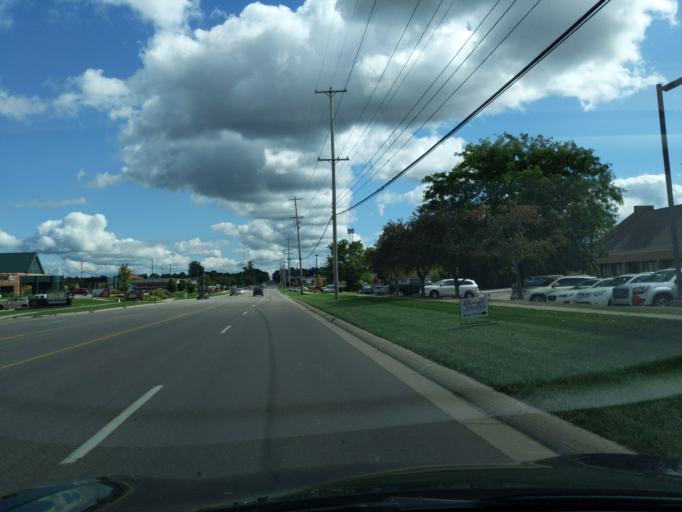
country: US
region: Michigan
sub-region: Ingham County
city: Okemos
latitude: 42.6829
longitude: -84.4377
